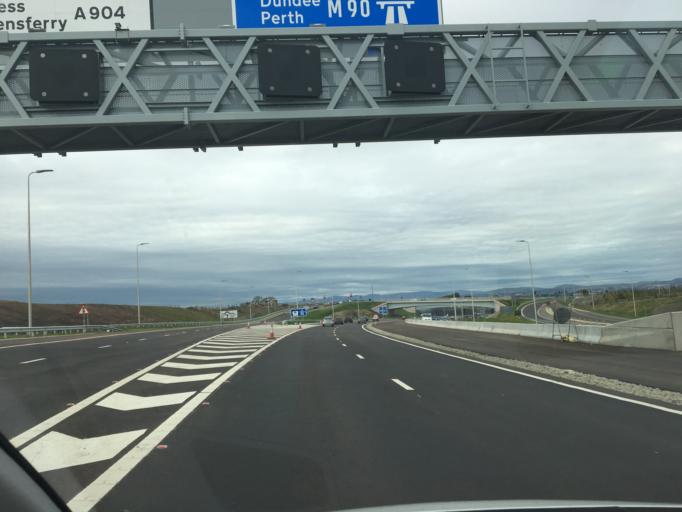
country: GB
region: Scotland
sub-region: Edinburgh
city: Queensferry
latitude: 55.9822
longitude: -3.4189
